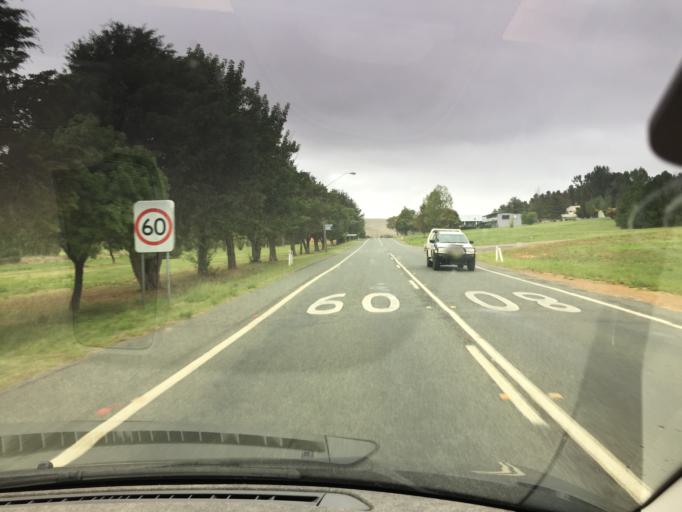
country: AU
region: New South Wales
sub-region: Cooma-Monaro
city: Cooma
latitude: -36.2232
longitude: 149.1342
